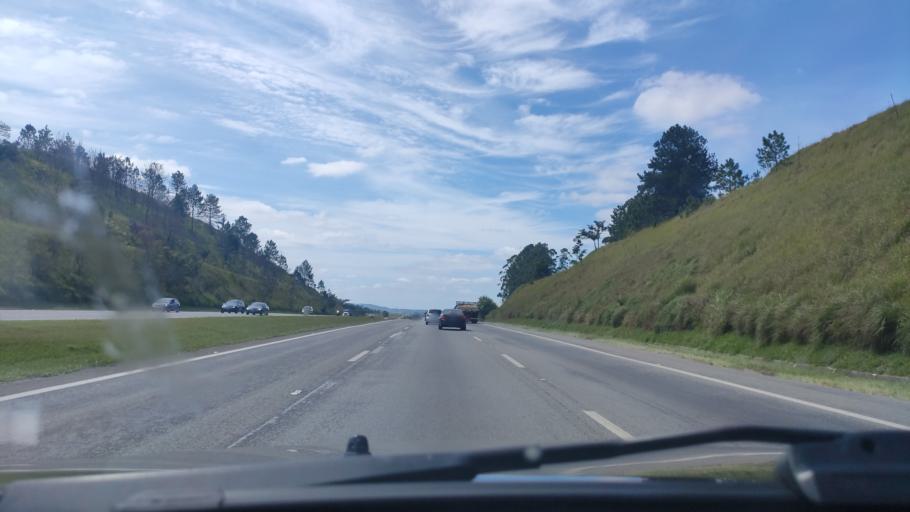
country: BR
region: Sao Paulo
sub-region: Aruja
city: Aruja
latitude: -23.4432
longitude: -46.2676
